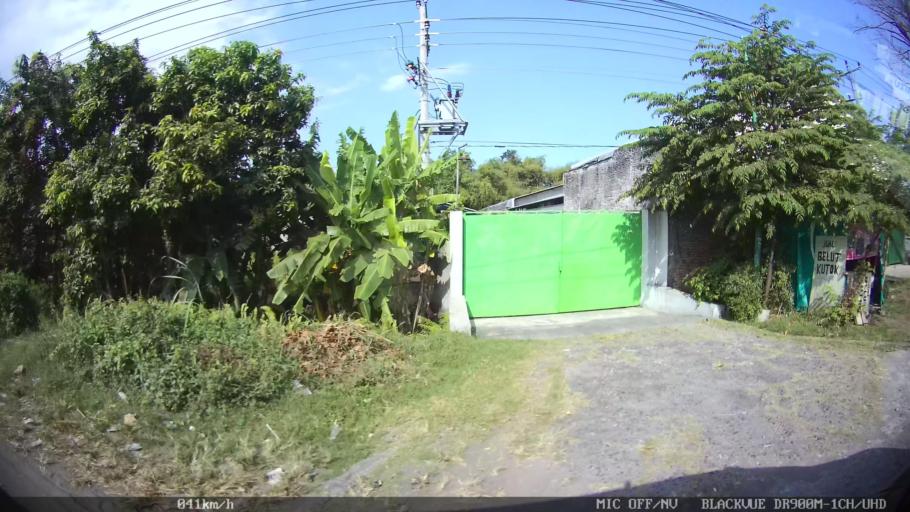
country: ID
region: Daerah Istimewa Yogyakarta
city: Sewon
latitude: -7.8499
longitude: 110.3746
